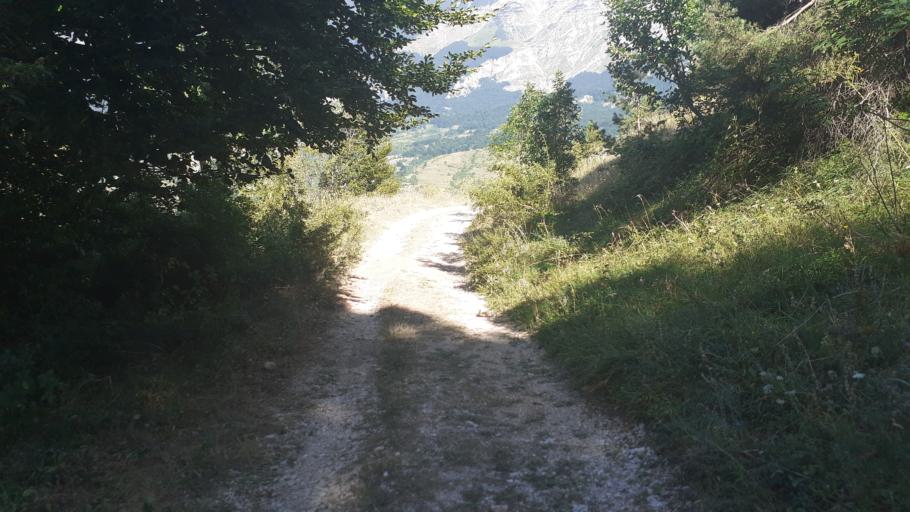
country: IT
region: Abruzzo
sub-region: Provincia di Pescara
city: Sant'Eufemia a Maiella
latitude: 42.1044
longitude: 14.0075
